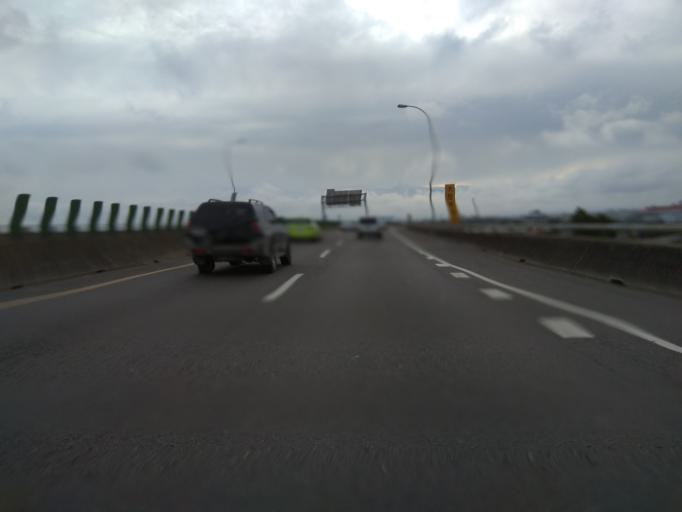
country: TW
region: Taiwan
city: Daxi
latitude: 24.9253
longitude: 121.2191
